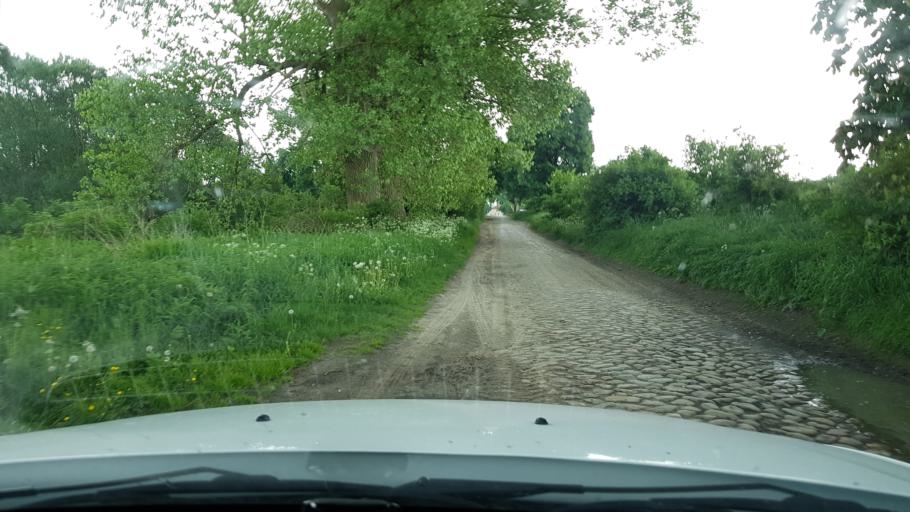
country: PL
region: West Pomeranian Voivodeship
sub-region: Powiat stargardzki
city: Marianowo
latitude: 53.3429
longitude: 15.1881
